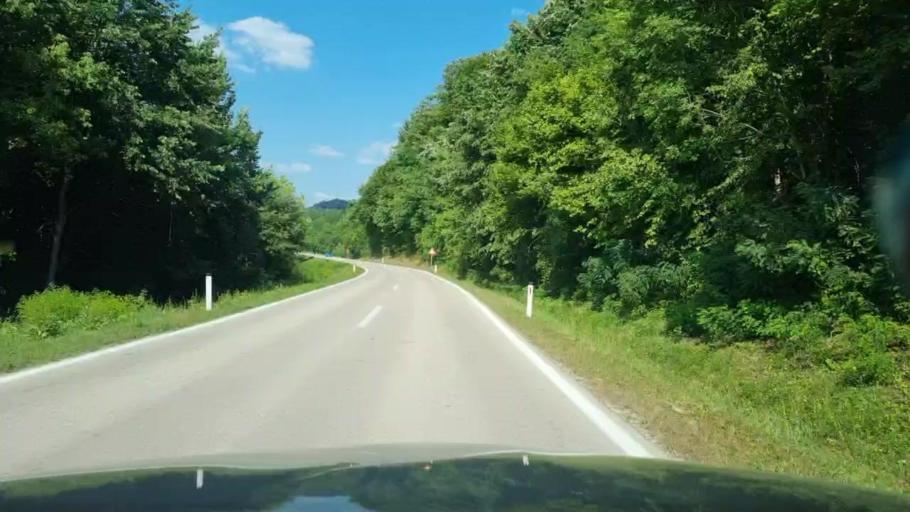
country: HR
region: Brodsko-Posavska
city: Garcin
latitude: 45.0836
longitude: 18.2101
